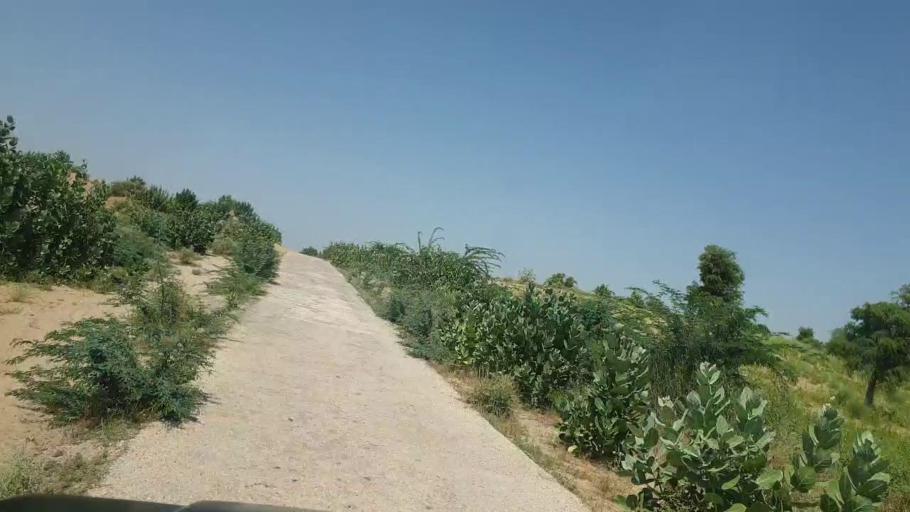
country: PK
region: Sindh
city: Chor
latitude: 25.3980
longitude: 70.3125
